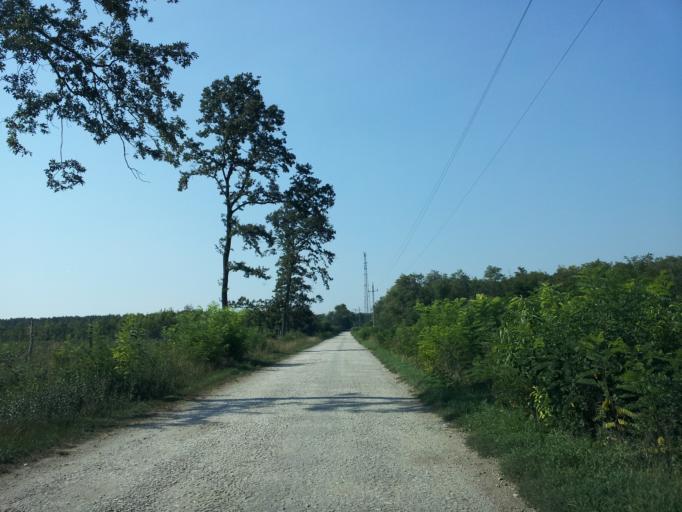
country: HU
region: Fejer
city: Polgardi
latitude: 47.0268
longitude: 18.2780
